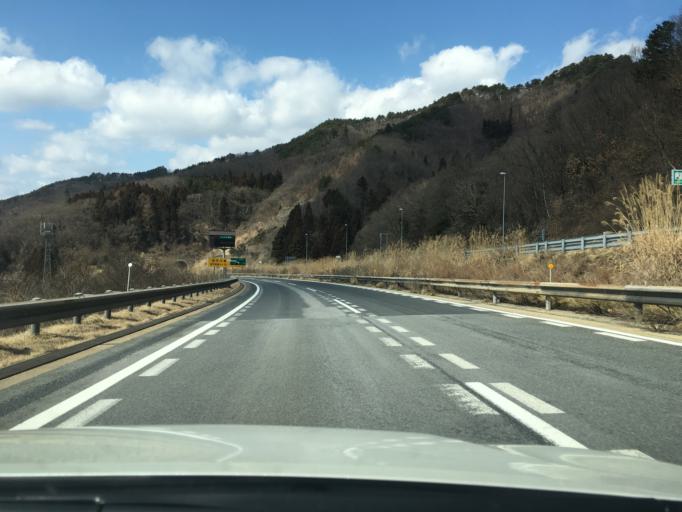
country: JP
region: Yamagata
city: Yamagata-shi
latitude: 38.2423
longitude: 140.4046
